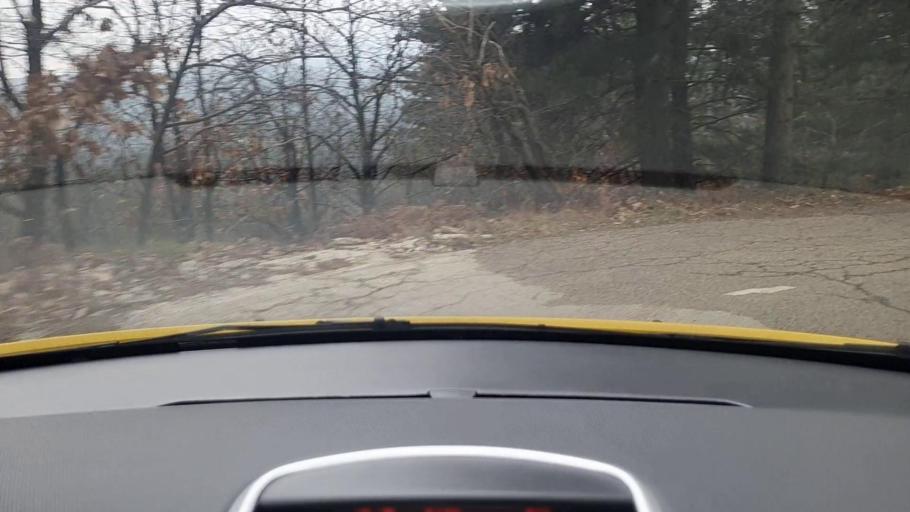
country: FR
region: Languedoc-Roussillon
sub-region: Departement du Gard
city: Besseges
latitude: 44.3581
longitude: 4.0222
